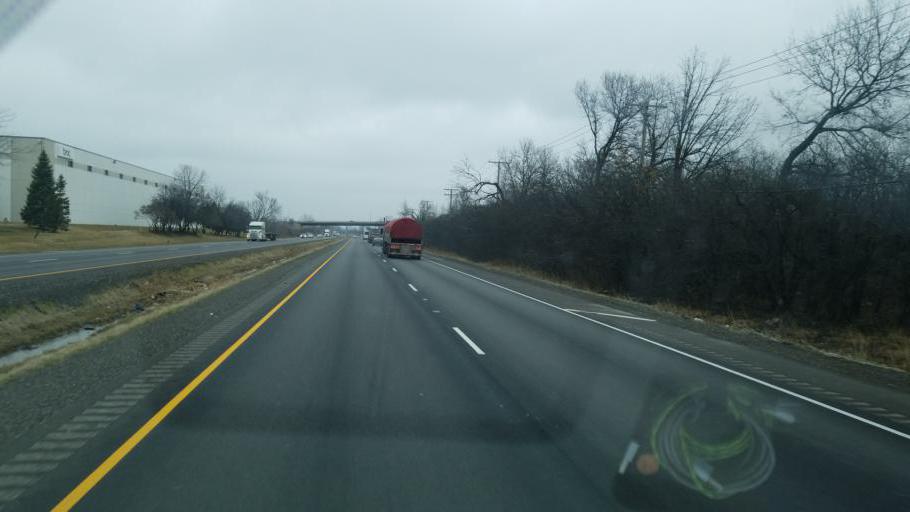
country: US
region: Illinois
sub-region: Lake County
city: Park City
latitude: 42.3303
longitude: -87.8835
